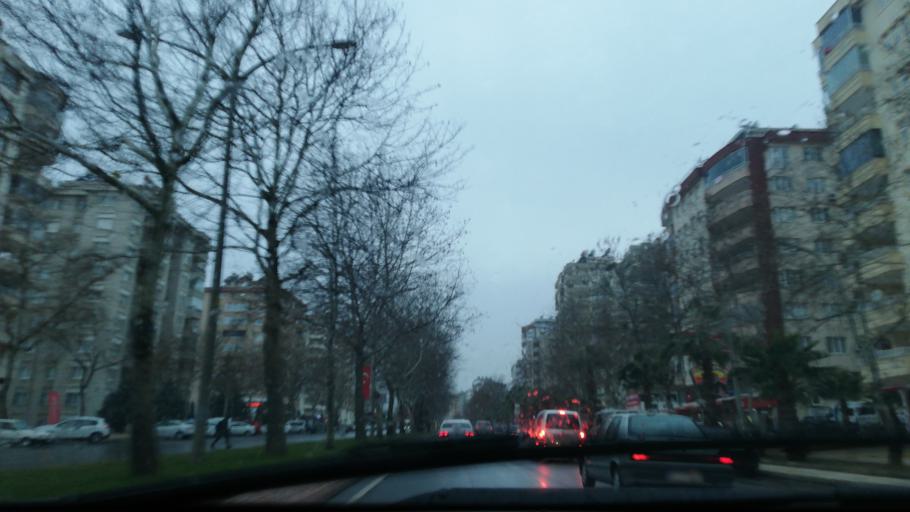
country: TR
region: Kahramanmaras
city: Kahramanmaras
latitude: 37.5876
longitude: 36.8923
